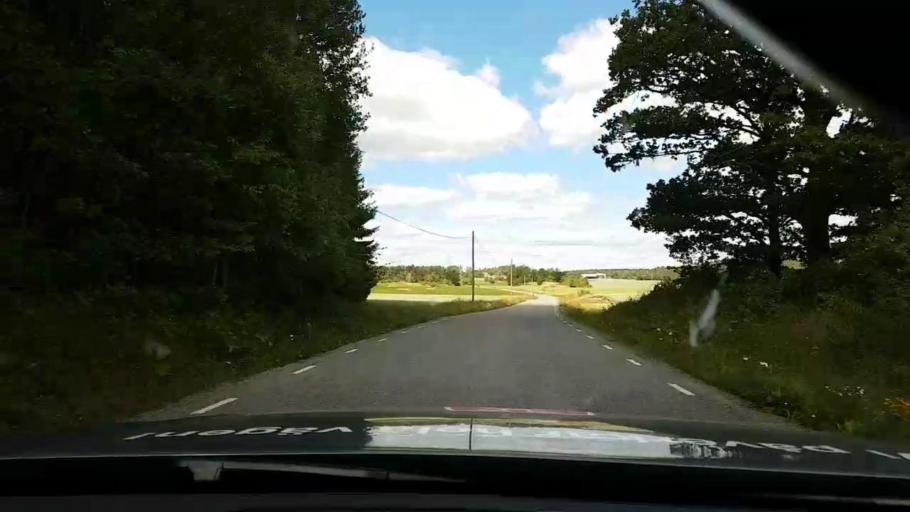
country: SE
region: Kalmar
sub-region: Vasterviks Kommun
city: Forserum
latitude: 58.0008
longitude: 16.5912
